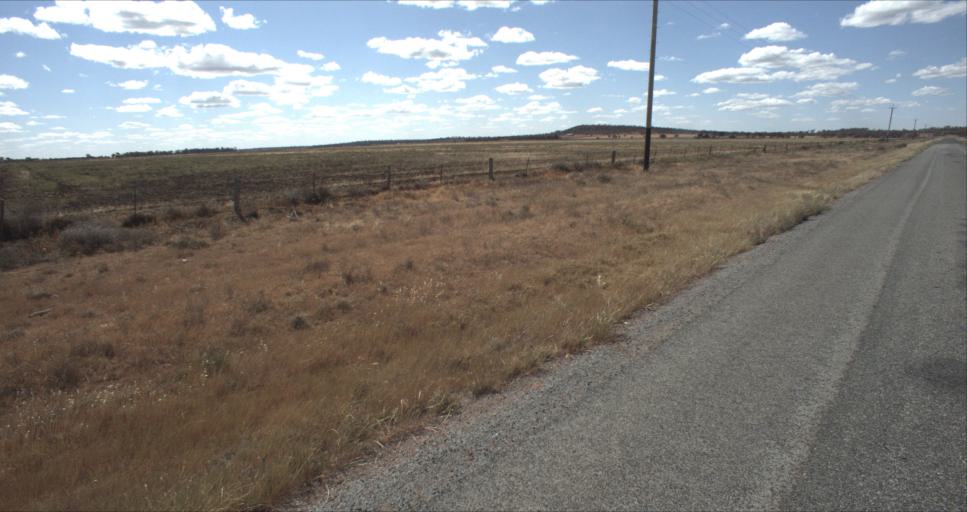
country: AU
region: New South Wales
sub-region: Leeton
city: Leeton
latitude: -34.4405
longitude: 146.2565
